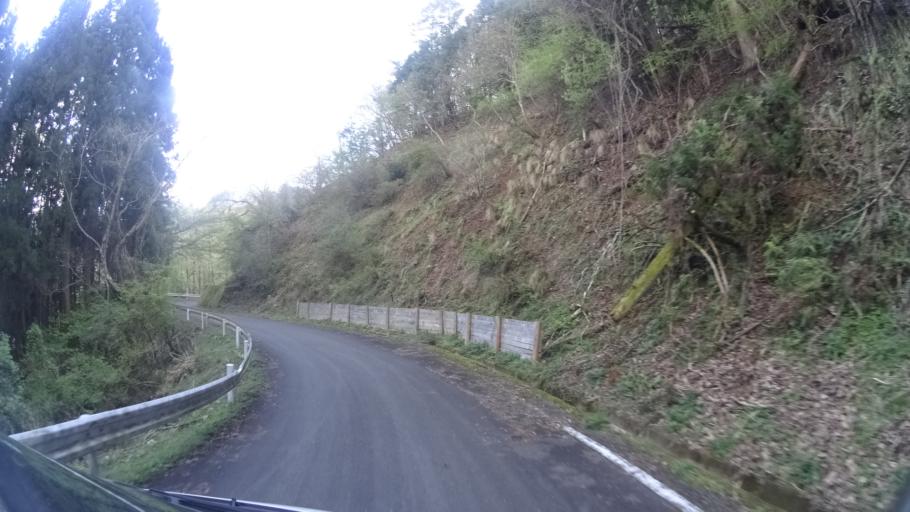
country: JP
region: Kyoto
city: Ayabe
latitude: 35.2557
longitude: 135.3277
